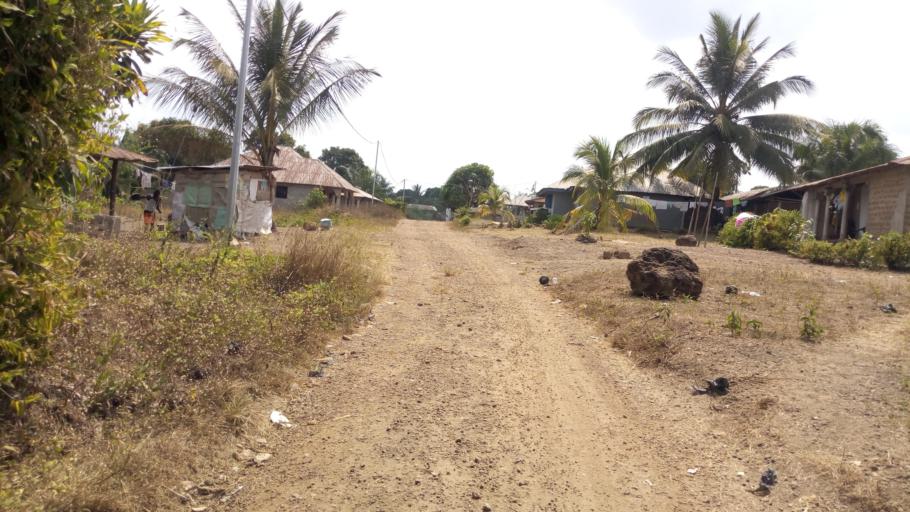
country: SL
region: Southern Province
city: Mogbwemo
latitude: 7.7929
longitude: -12.3029
